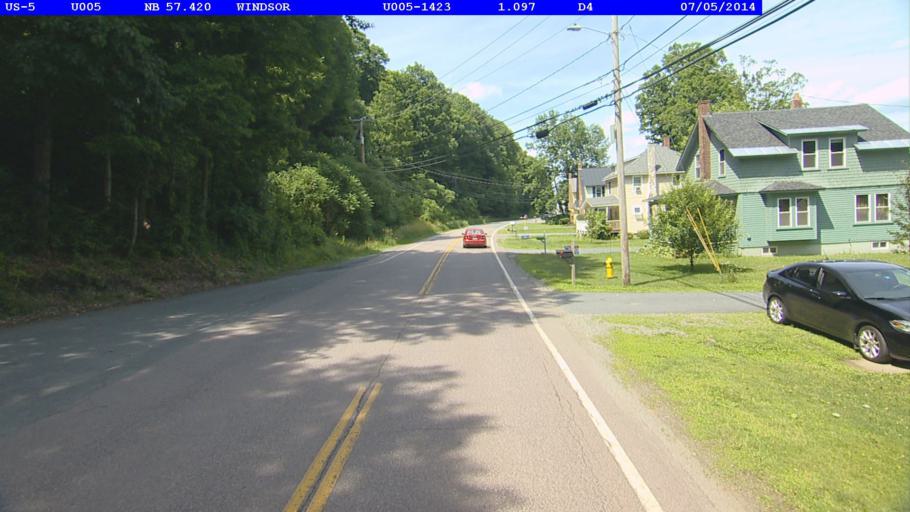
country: US
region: Vermont
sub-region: Windsor County
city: Windsor
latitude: 43.4443
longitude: -72.3981
